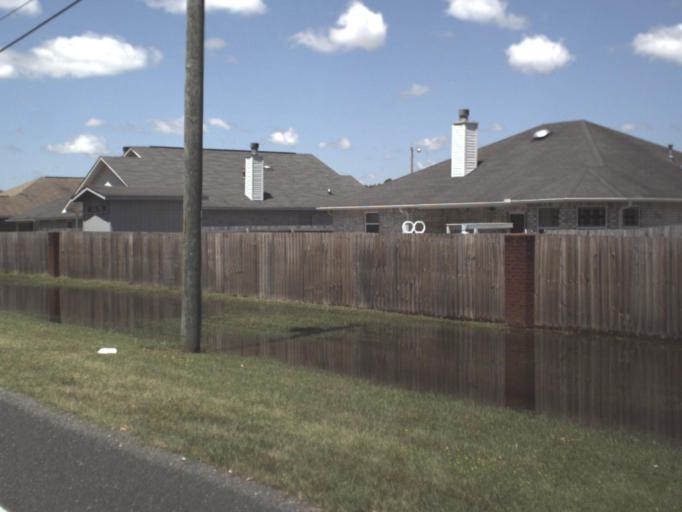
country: US
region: Florida
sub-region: Escambia County
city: Myrtle Grove
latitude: 30.3988
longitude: -87.3916
